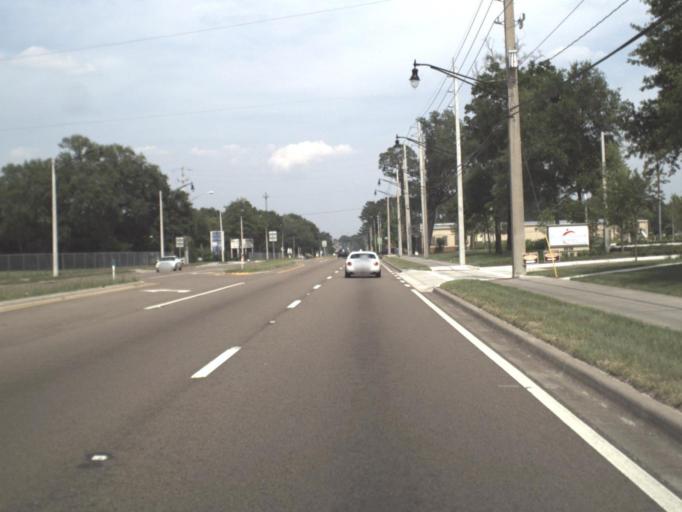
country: US
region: Florida
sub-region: Clay County
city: Bellair-Meadowbrook Terrace
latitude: 30.2477
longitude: -81.8084
